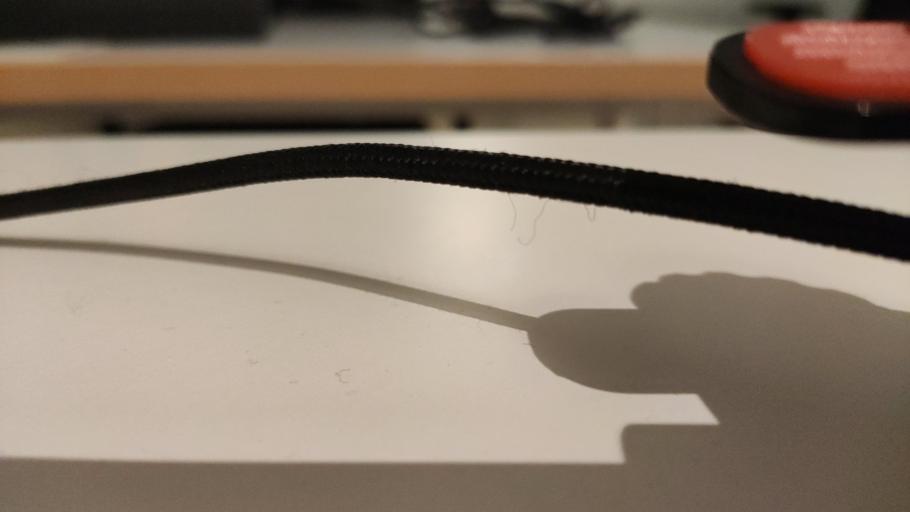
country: RU
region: Moskovskaya
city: Rogachevo
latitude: 56.4302
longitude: 37.1809
